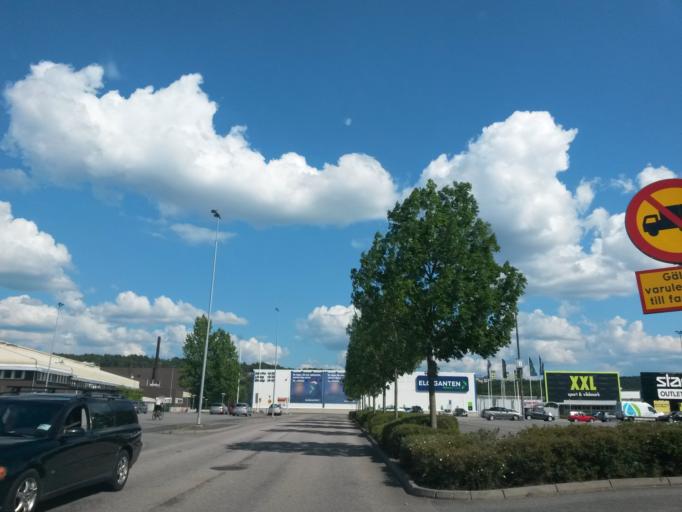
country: SE
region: Vaestra Goetaland
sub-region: Goteborg
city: Hammarkullen
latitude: 57.7717
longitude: 11.9989
